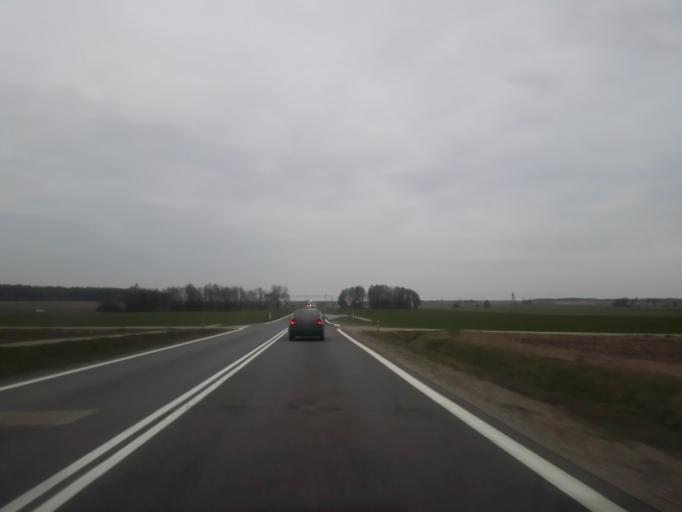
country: PL
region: Podlasie
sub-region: Powiat kolnenski
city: Stawiski
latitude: 53.4206
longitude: 22.1663
